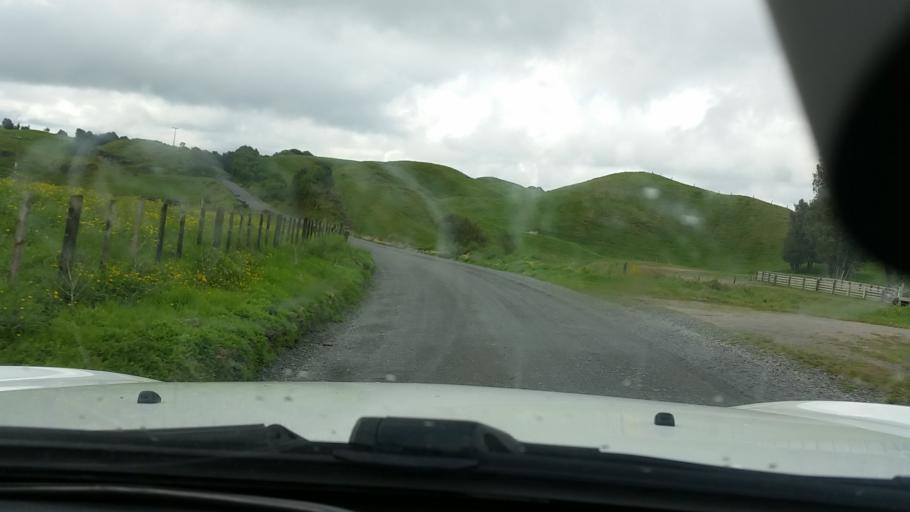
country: NZ
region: Bay of Plenty
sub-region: Rotorua District
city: Rotorua
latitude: -38.1389
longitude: 176.0795
